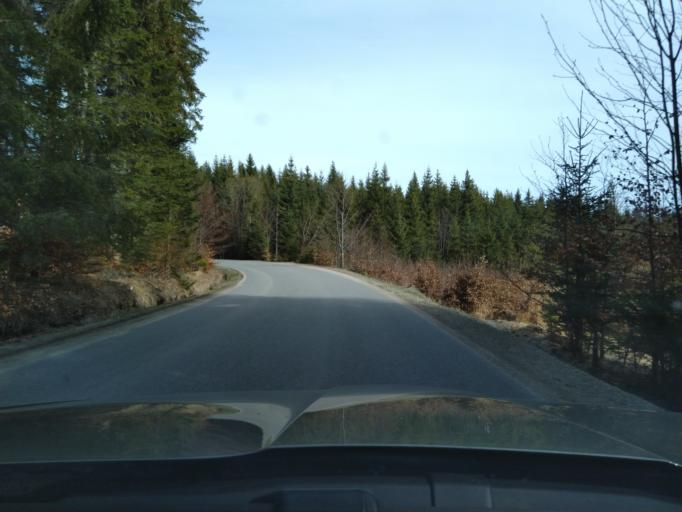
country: CZ
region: Jihocesky
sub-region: Okres Prachatice
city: Stachy
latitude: 49.0634
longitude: 13.6557
